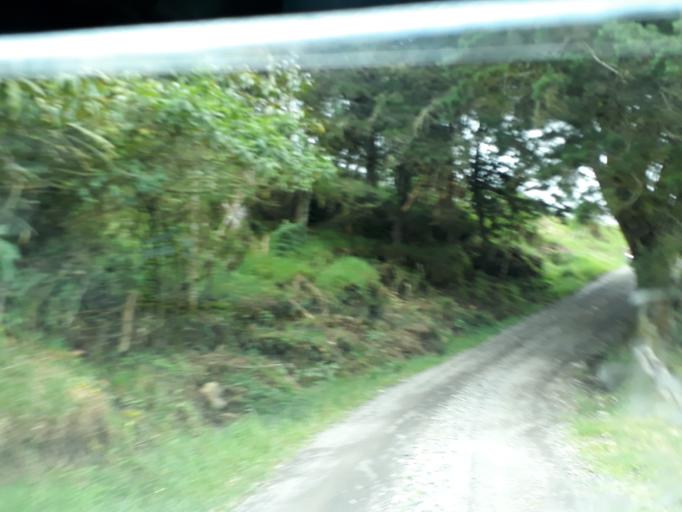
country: CO
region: Cundinamarca
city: Carmen de Carupa
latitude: 5.3751
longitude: -73.9750
